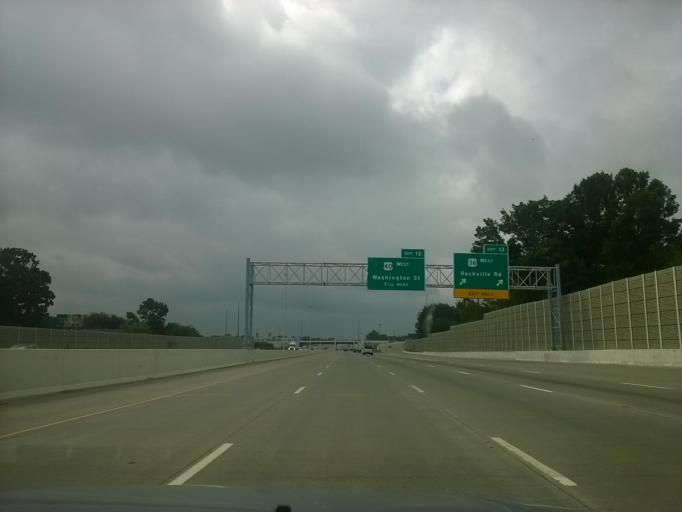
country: US
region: Indiana
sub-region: Marion County
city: Speedway
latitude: 39.7697
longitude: -86.2690
